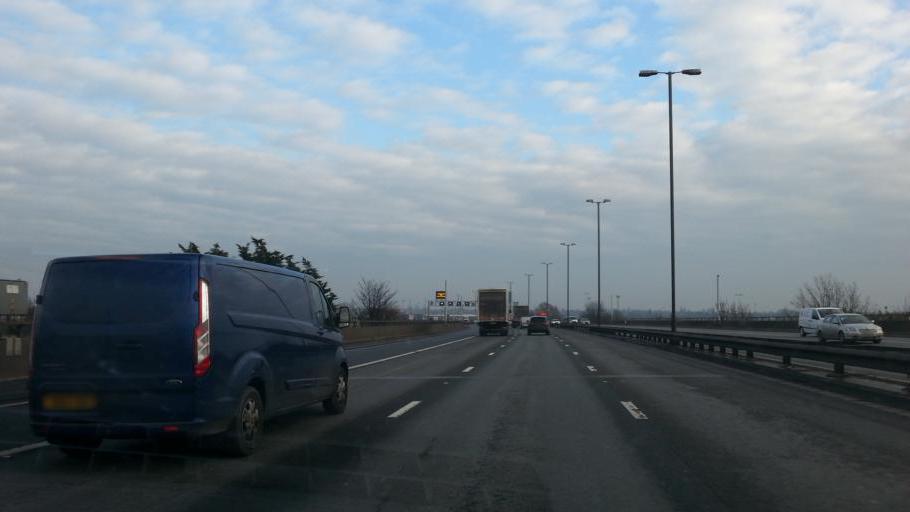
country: GB
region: England
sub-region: City and Borough of Birmingham
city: Birmingham
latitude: 52.5054
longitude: -1.8493
